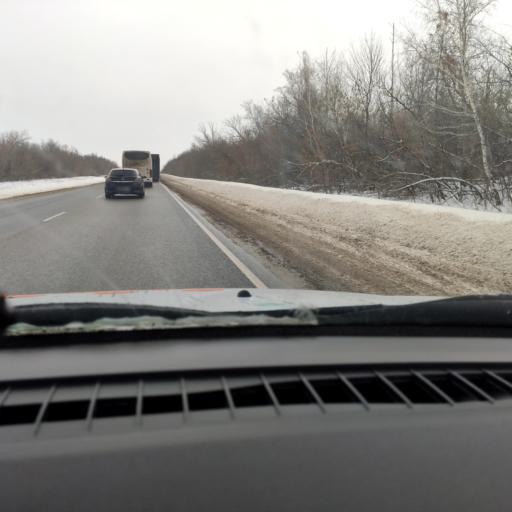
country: RU
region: Samara
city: Dubovyy Umet
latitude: 52.9880
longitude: 50.2631
